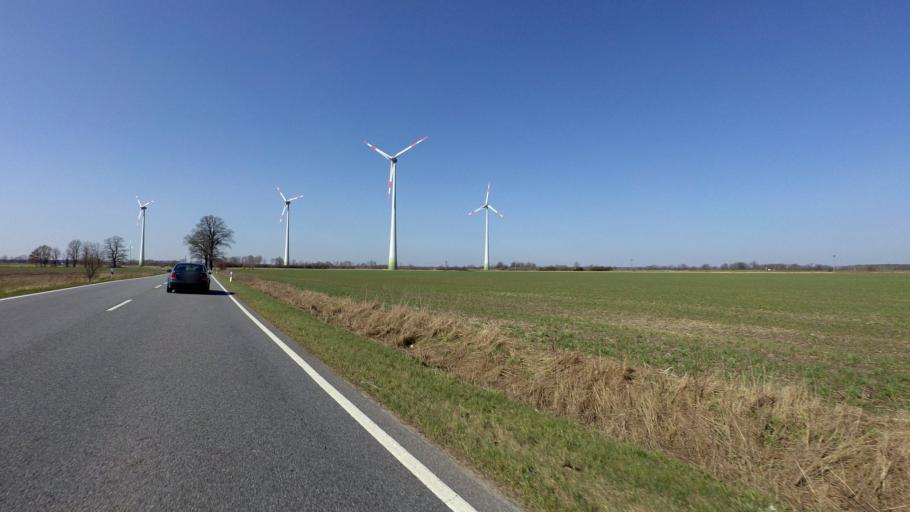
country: DE
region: Brandenburg
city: Ruthnick
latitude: 52.9011
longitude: 13.0222
